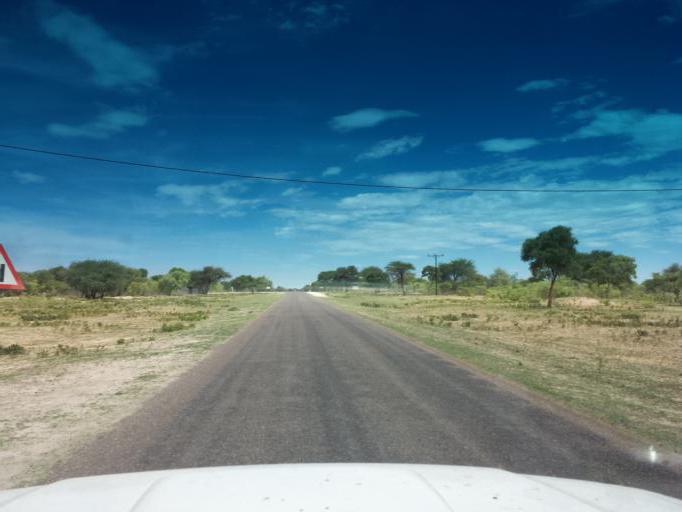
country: BW
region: North West
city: Shakawe
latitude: -18.7471
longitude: 22.1718
